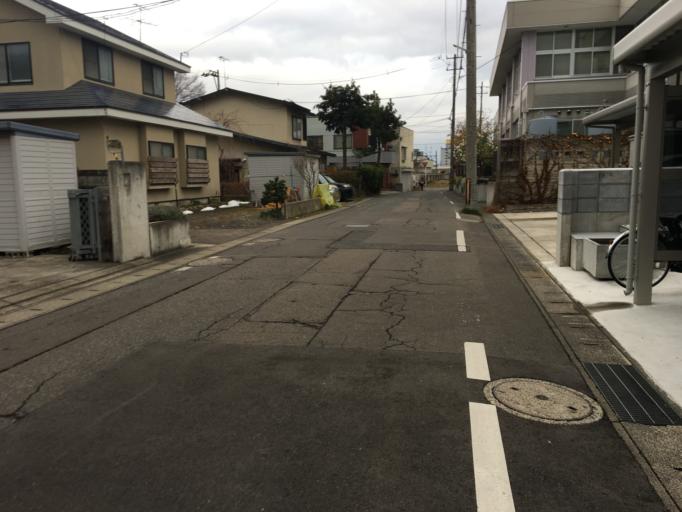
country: JP
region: Aomori
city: Hirosaki
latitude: 40.5953
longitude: 140.4703
